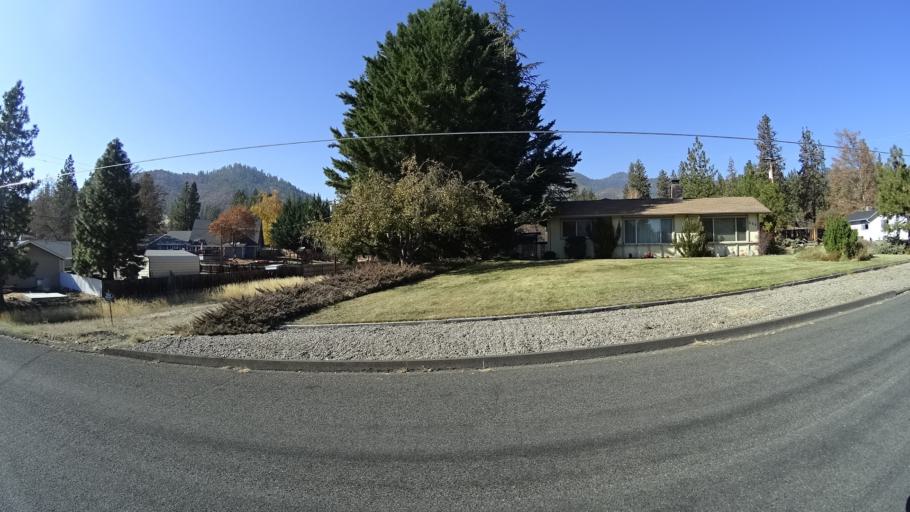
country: US
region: California
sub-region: Siskiyou County
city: Yreka
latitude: 41.7330
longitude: -122.6510
